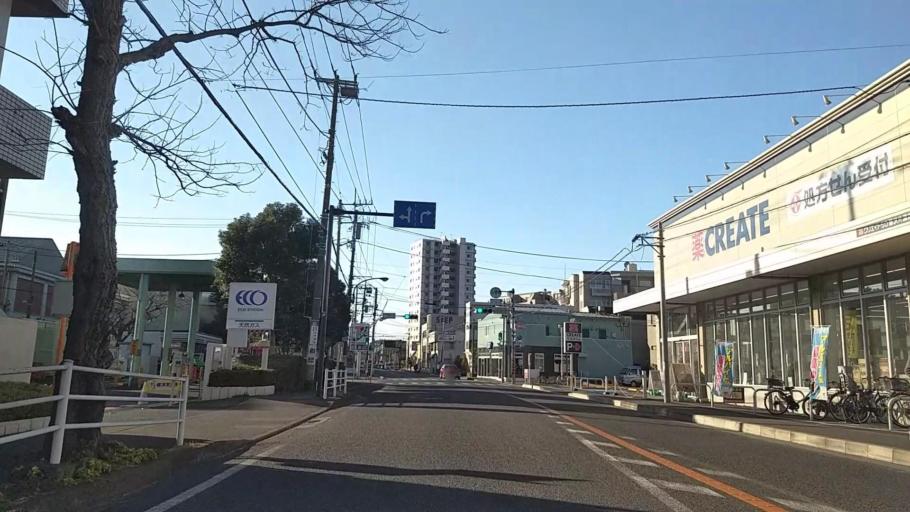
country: JP
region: Kanagawa
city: Fujisawa
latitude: 35.3306
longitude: 139.4880
